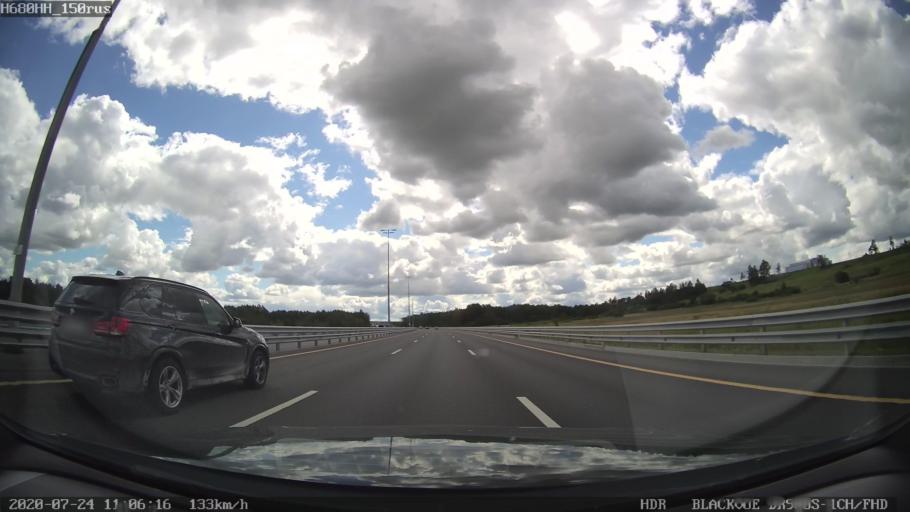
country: RU
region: St.-Petersburg
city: Shushary
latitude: 59.7655
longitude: 30.3705
